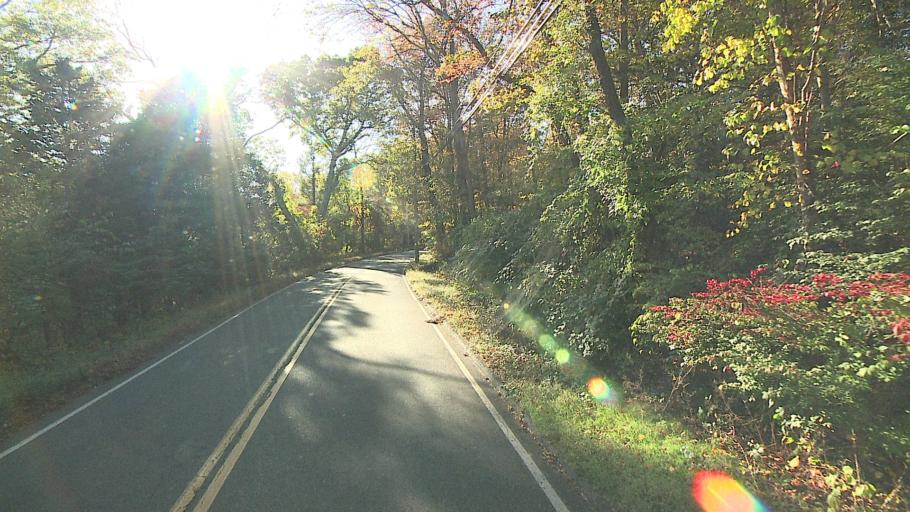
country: US
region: Connecticut
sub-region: Fairfield County
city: Wilton
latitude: 41.1939
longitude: -73.3980
